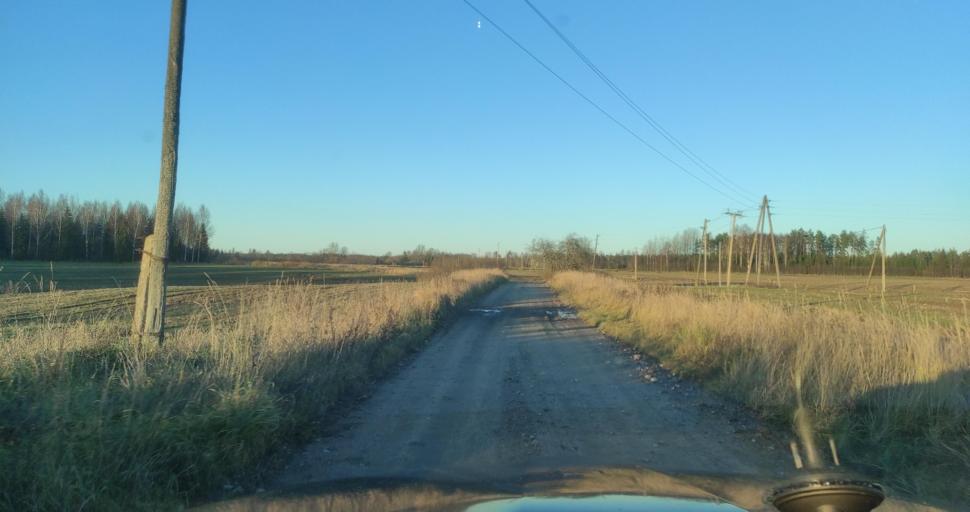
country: LV
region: Dundaga
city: Dundaga
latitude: 57.3860
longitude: 22.0882
